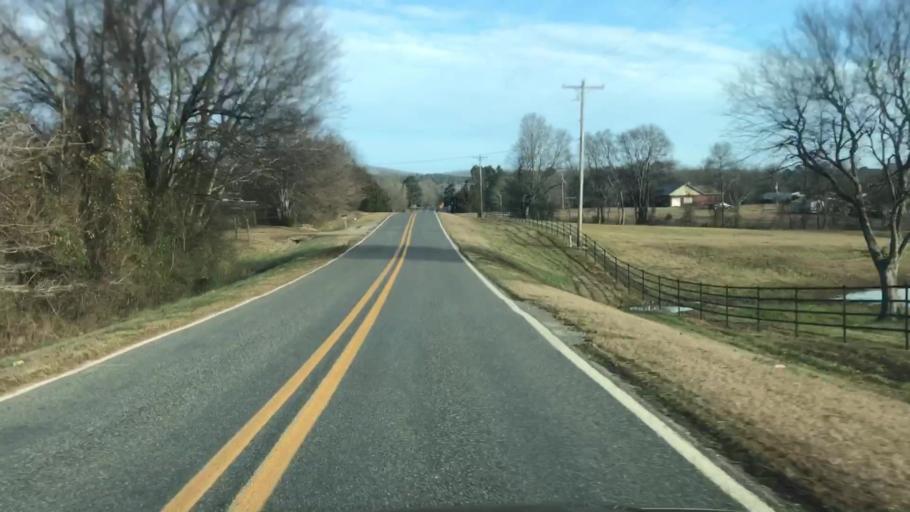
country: US
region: Arkansas
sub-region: Garland County
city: Rockwell
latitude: 34.5036
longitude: -93.2762
